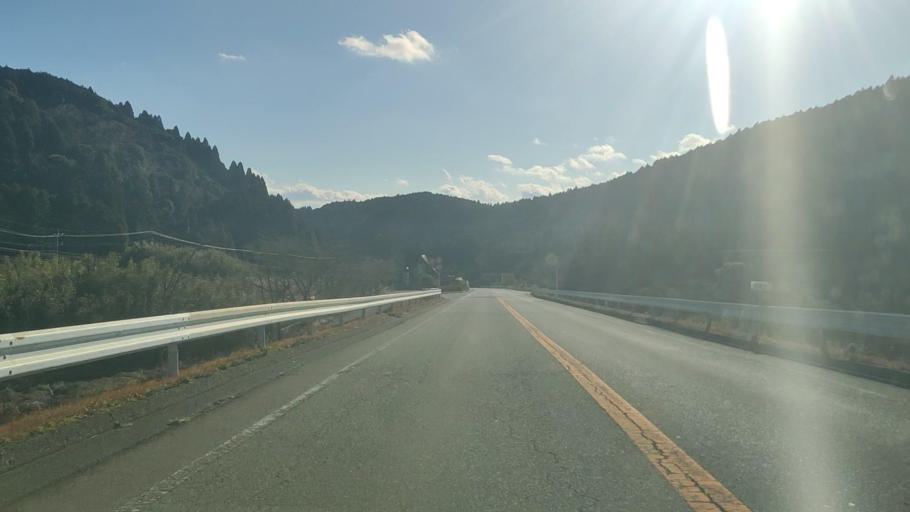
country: JP
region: Fukuoka
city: Maebaru-chuo
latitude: 33.4617
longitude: 130.2747
